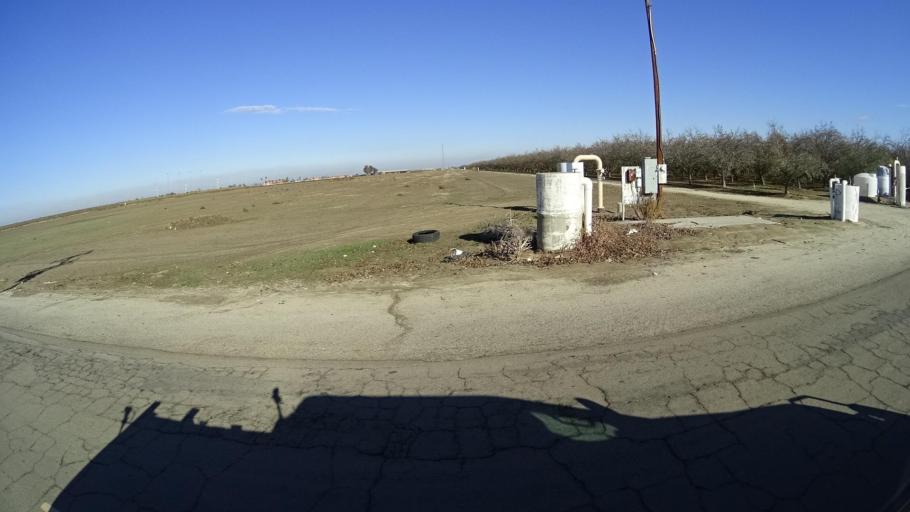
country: US
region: California
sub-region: Kern County
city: Delano
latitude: 35.7324
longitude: -119.2675
